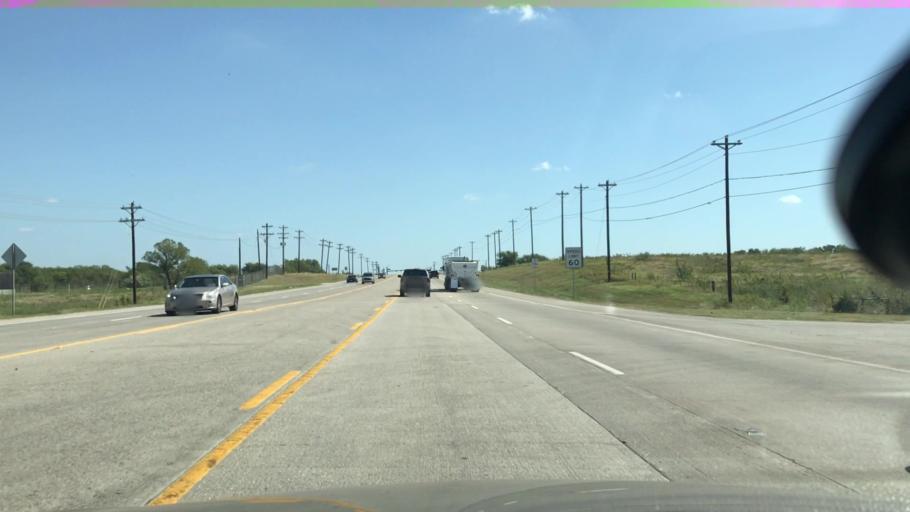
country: US
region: Texas
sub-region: Denton County
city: Little Elm
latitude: 33.2193
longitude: -96.8876
